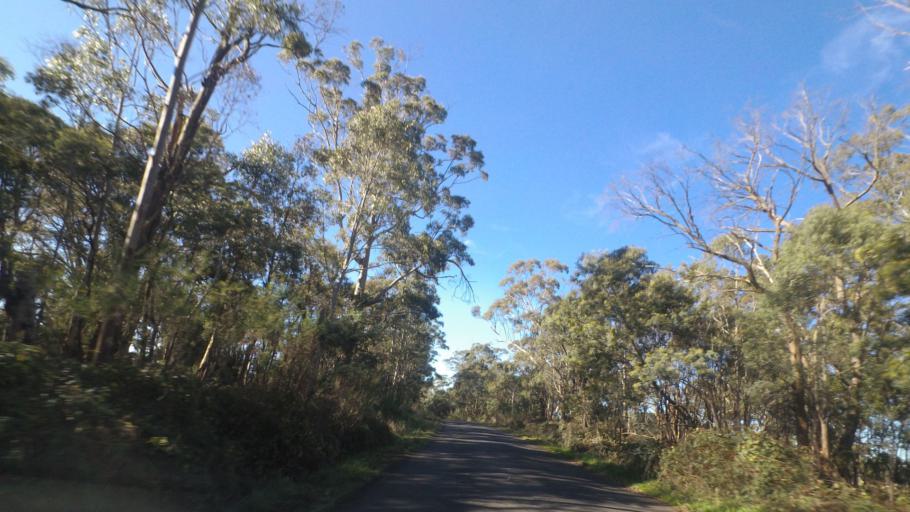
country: AU
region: Victoria
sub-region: Mount Alexander
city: Castlemaine
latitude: -37.3215
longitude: 144.3236
